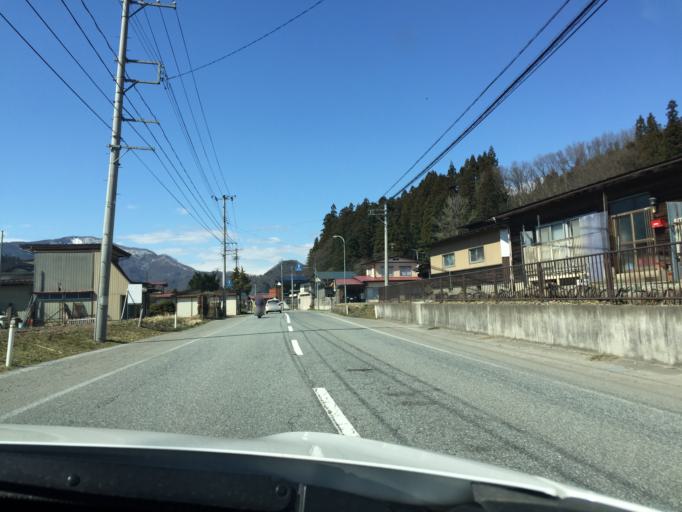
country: JP
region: Yamagata
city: Nagai
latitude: 38.2105
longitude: 140.0995
